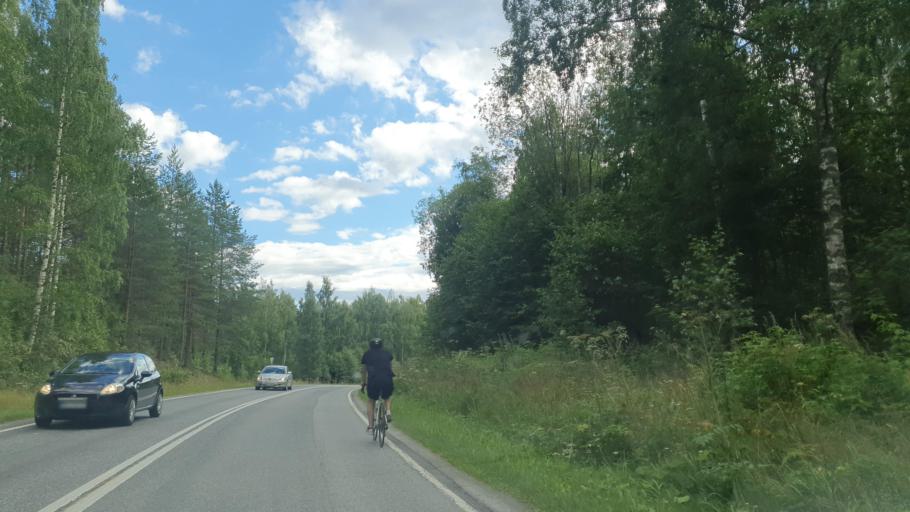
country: FI
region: Central Finland
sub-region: Jyvaeskylae
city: Saeynaetsalo
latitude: 62.1447
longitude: 25.7193
